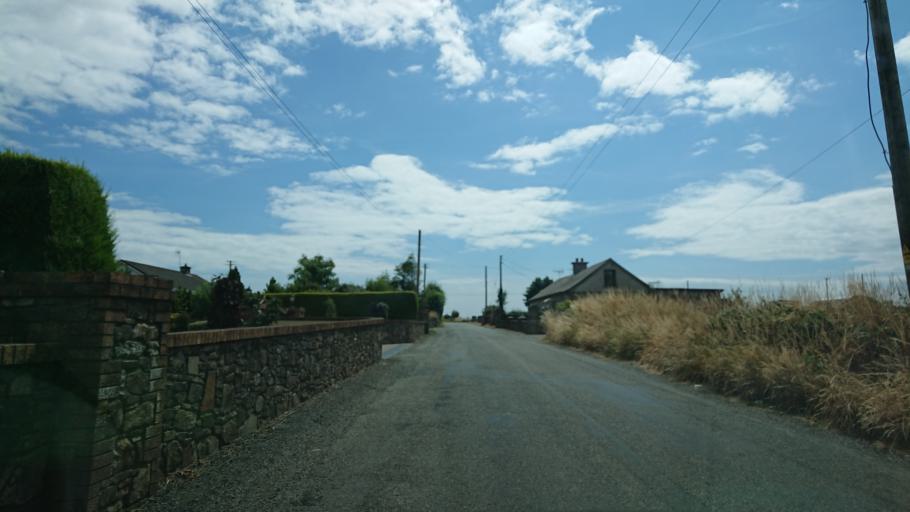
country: IE
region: Munster
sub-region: Waterford
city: Portlaw
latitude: 52.1996
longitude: -7.3284
